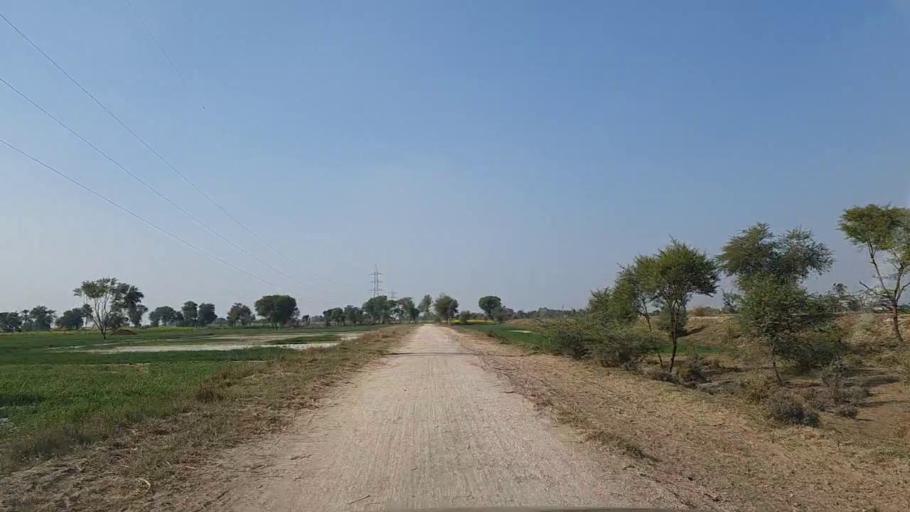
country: PK
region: Sindh
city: Daur
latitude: 26.3834
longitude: 68.3277
